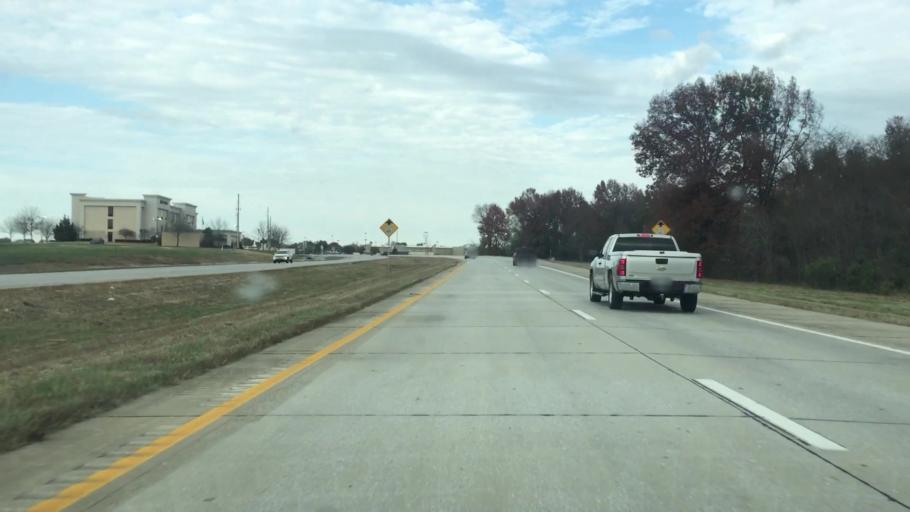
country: US
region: Missouri
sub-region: Henry County
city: Clinton
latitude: 38.3584
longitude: -93.7538
